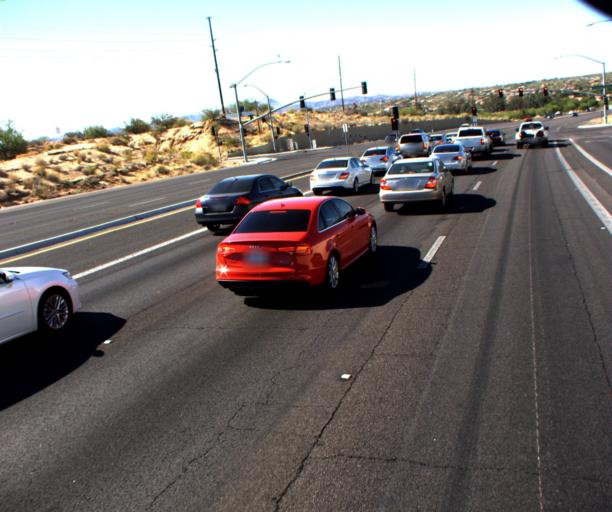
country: US
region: Arizona
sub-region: Pima County
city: Oro Valley
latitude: 32.3874
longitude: -110.9643
